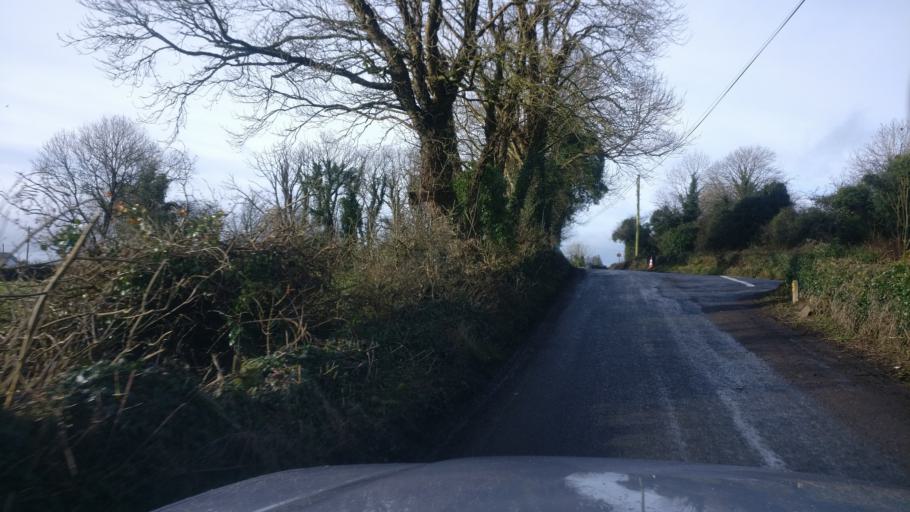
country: IE
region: Connaught
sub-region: County Galway
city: Loughrea
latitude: 53.1999
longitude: -8.6624
